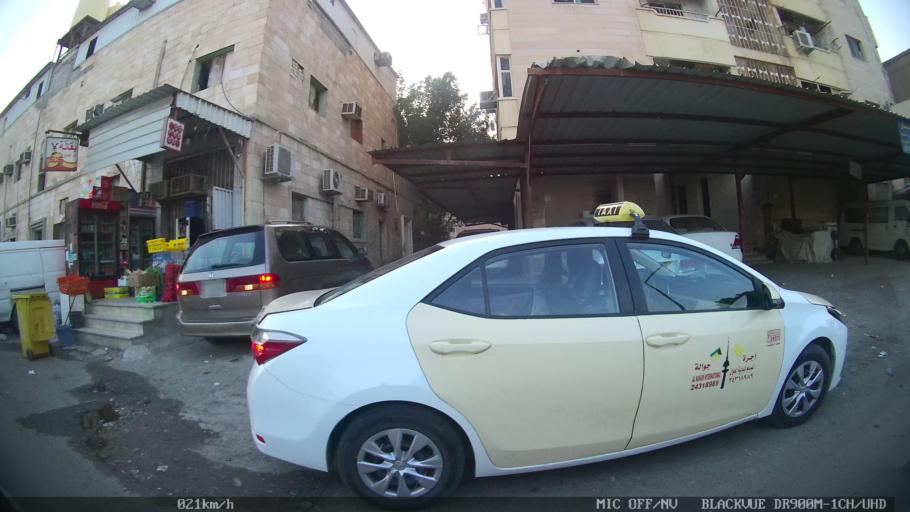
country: KW
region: Al Farwaniyah
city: Janub as Surrah
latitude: 29.2940
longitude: 47.9783
